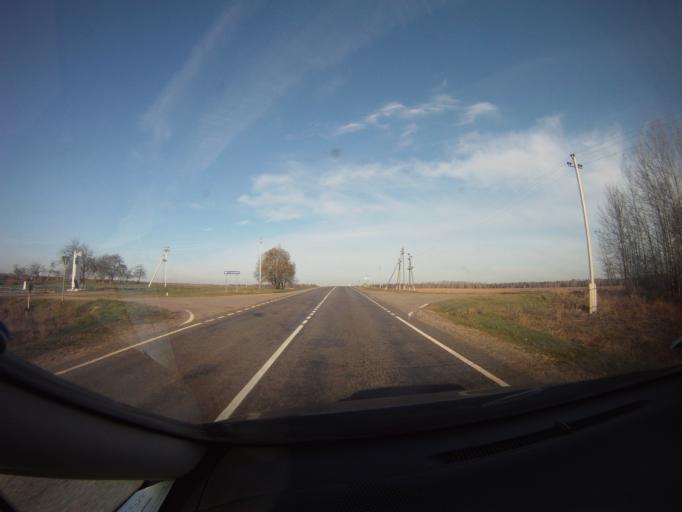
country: BY
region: Minsk
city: Il'ya
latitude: 54.3523
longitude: 27.4286
